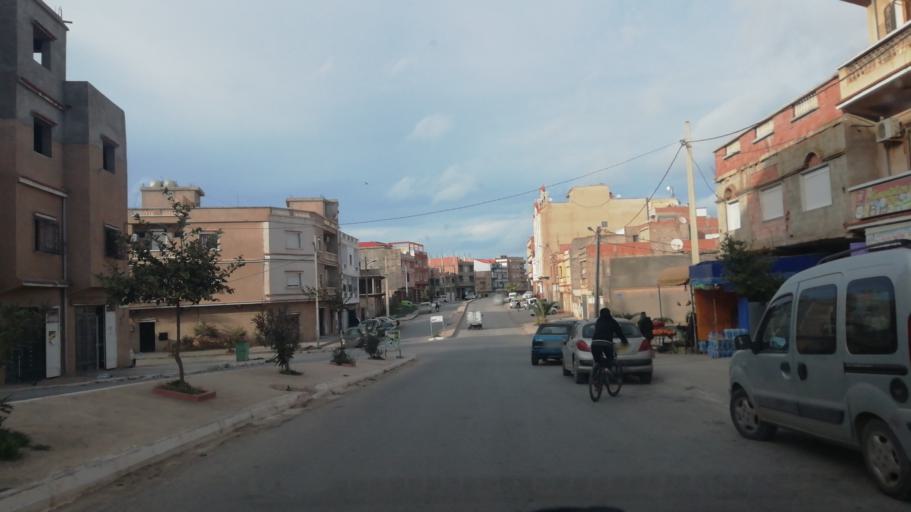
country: DZ
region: Oran
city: Bir el Djir
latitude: 35.7335
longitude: -0.5726
